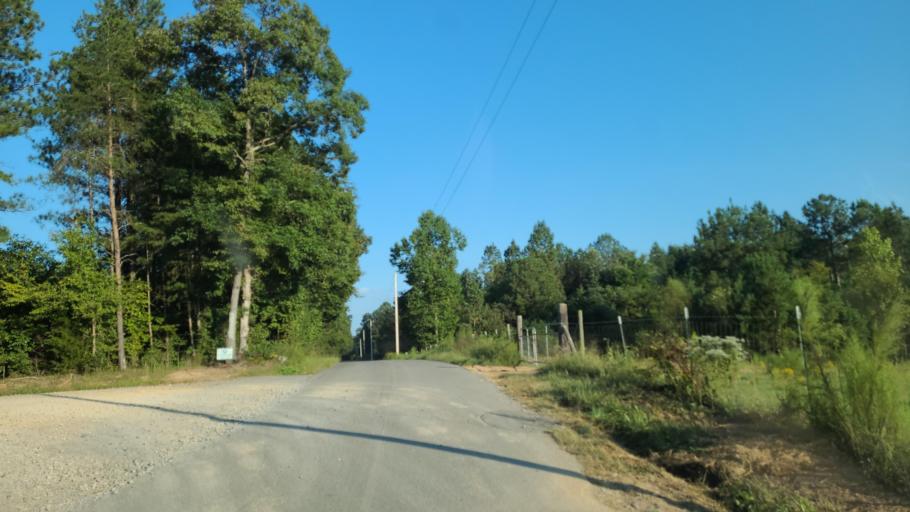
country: US
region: Tennessee
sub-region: Bradley County
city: Wildwood Lake
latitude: 35.0224
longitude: -84.7691
